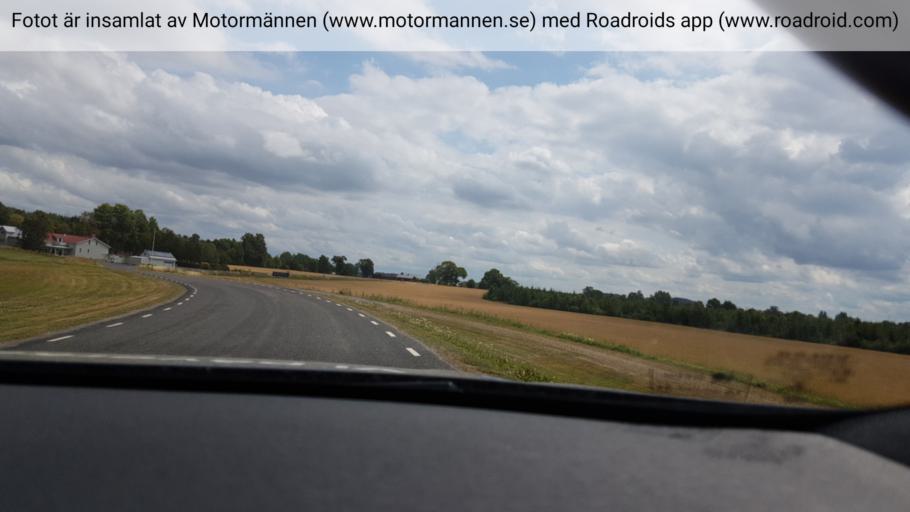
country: SE
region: Vaestra Goetaland
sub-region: Falkopings Kommun
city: Floby
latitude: 58.1249
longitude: 13.4214
